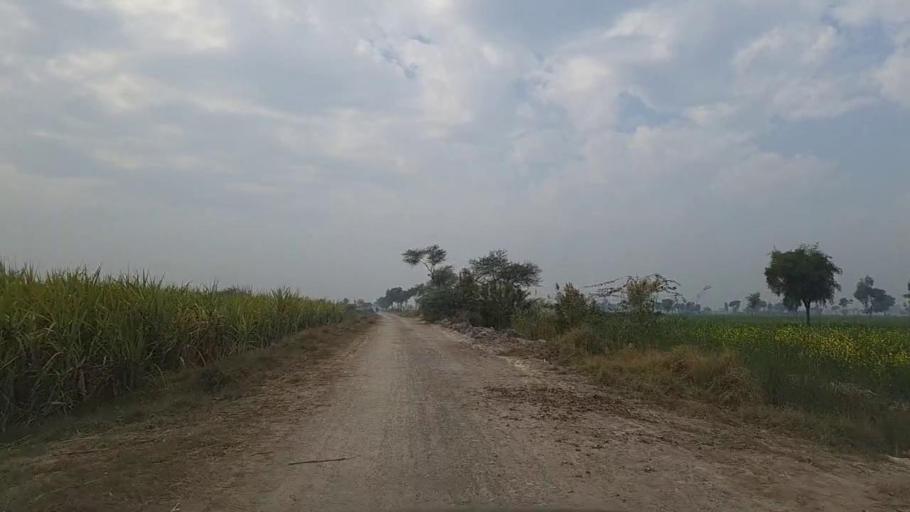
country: PK
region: Sindh
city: Nawabshah
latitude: 26.3606
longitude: 68.3962
